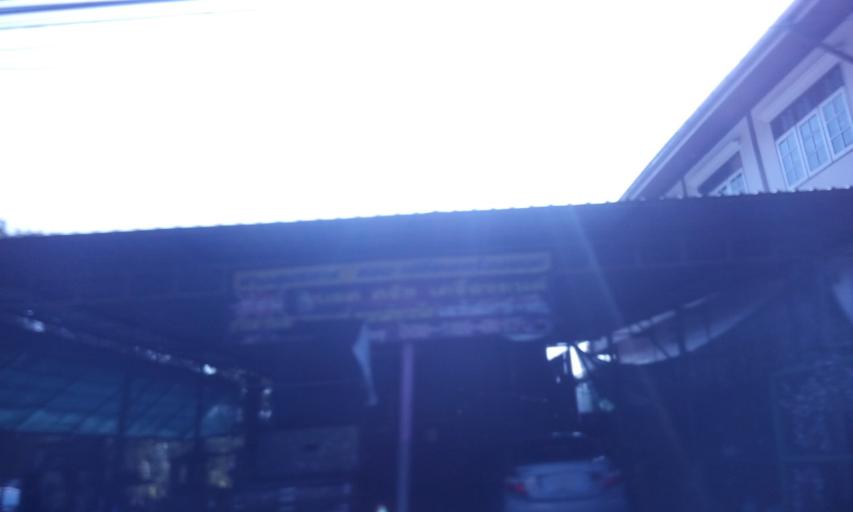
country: TH
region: Pathum Thani
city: Lam Luk Ka
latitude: 13.9566
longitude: 100.7058
